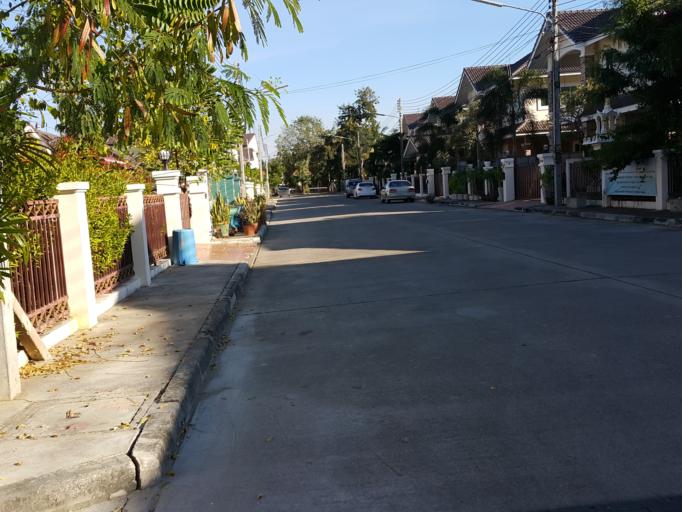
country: TH
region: Chiang Mai
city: San Kamphaeng
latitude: 18.7739
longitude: 99.0847
